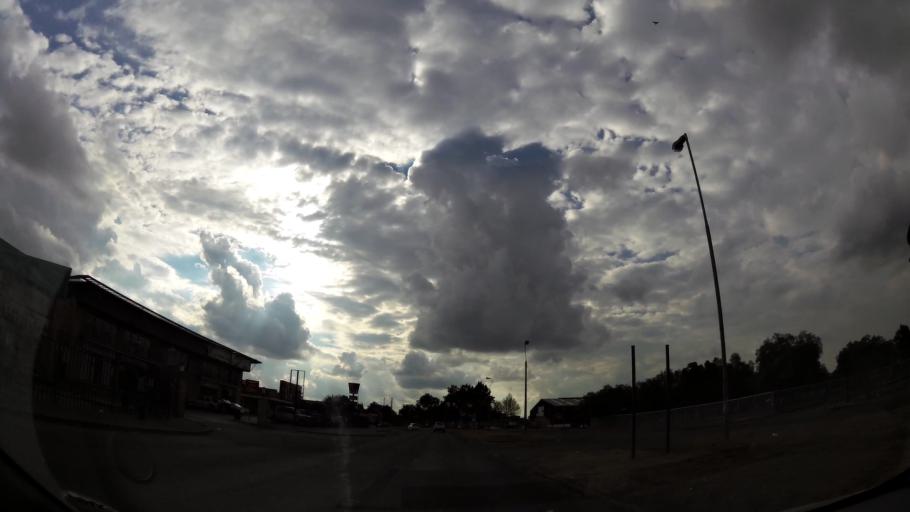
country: ZA
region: Orange Free State
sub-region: Fezile Dabi District Municipality
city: Sasolburg
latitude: -26.8212
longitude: 27.8347
